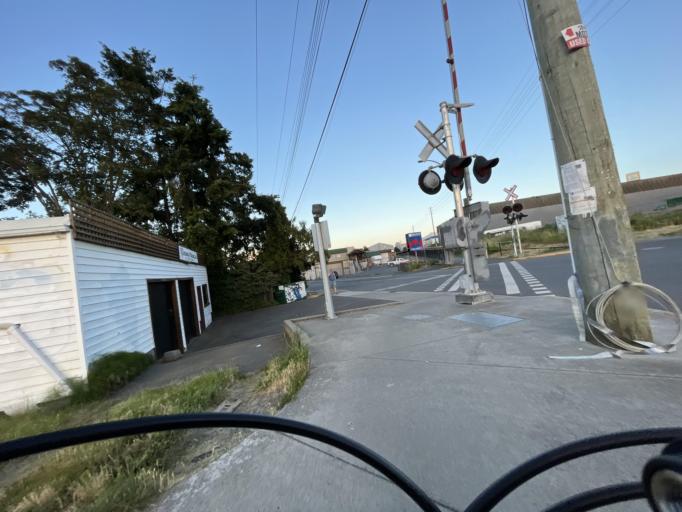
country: CA
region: British Columbia
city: Victoria
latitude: 48.4359
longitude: -123.3989
